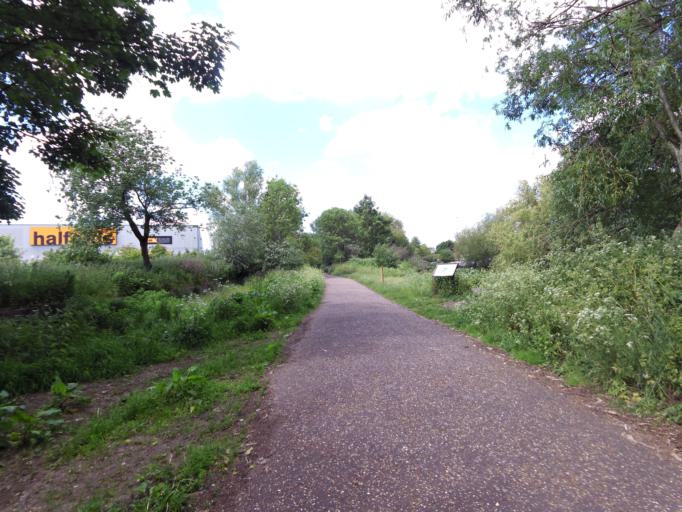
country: GB
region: England
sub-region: Norfolk
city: Norwich
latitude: 52.6359
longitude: 1.2874
